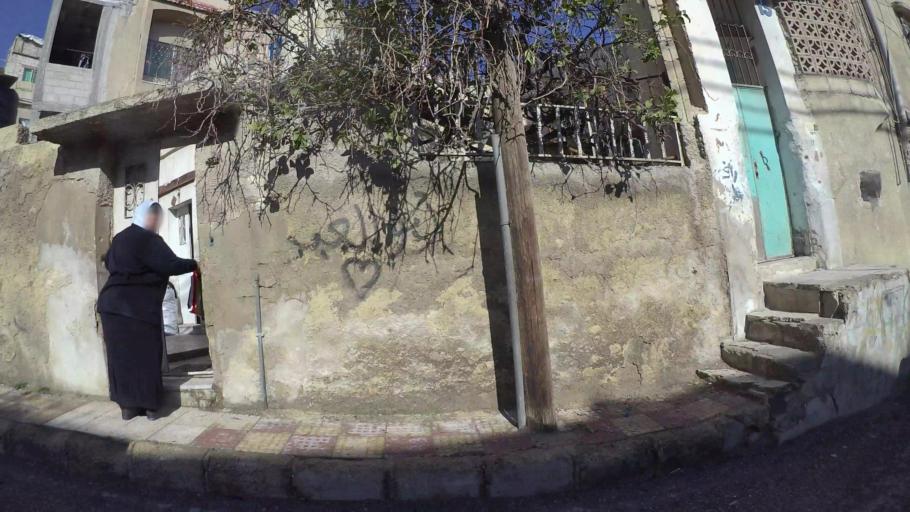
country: JO
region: Amman
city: Amman
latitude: 31.9886
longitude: 35.9903
